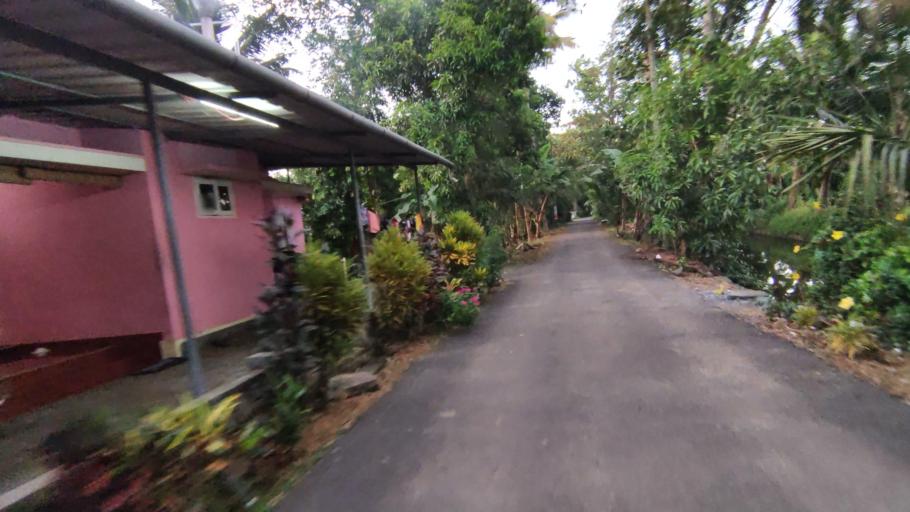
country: IN
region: Kerala
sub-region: Kottayam
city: Kottayam
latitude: 9.5791
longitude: 76.4538
